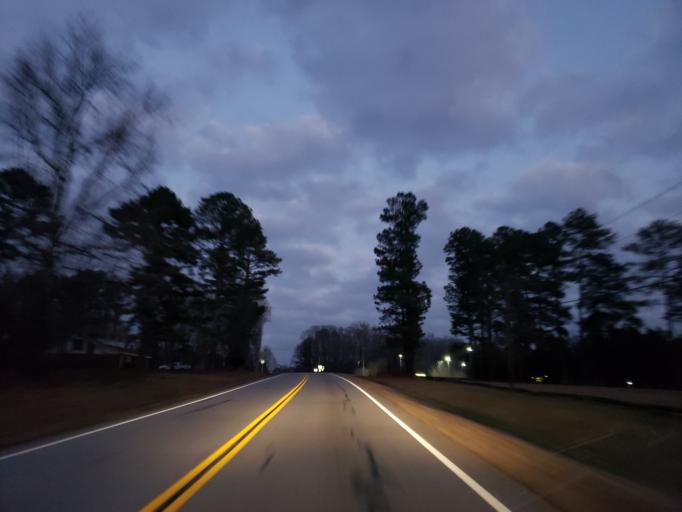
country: US
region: Georgia
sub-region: Carroll County
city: Temple
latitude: 33.8288
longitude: -85.0392
